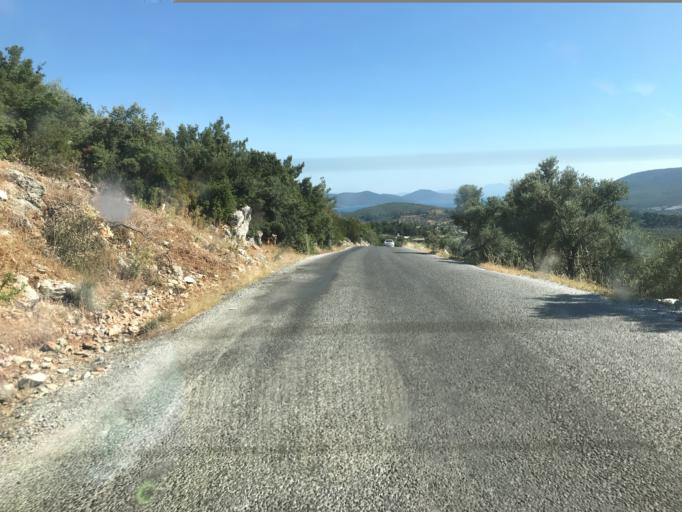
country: TR
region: Mugla
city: Selimiye
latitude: 37.3741
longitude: 27.4898
